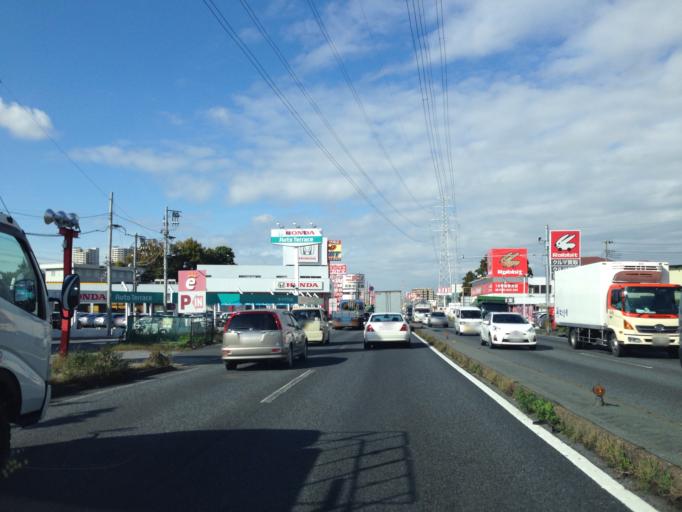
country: JP
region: Chiba
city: Kashiwa
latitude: 35.8850
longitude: 139.9636
